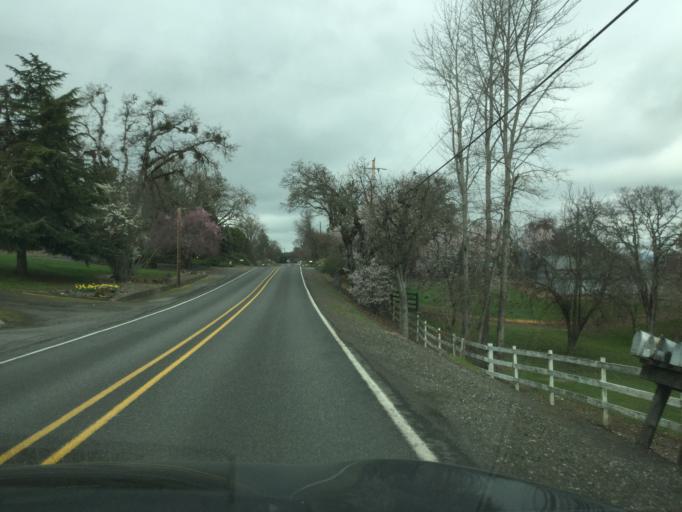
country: US
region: Oregon
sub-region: Jackson County
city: Central Point
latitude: 42.3773
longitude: -122.9572
